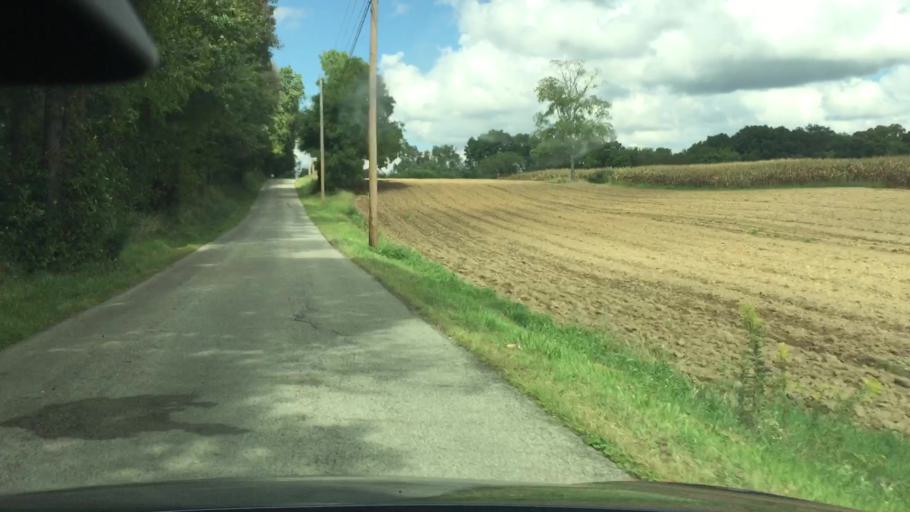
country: US
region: Pennsylvania
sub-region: Butler County
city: Nixon
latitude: 40.7551
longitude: -79.8851
